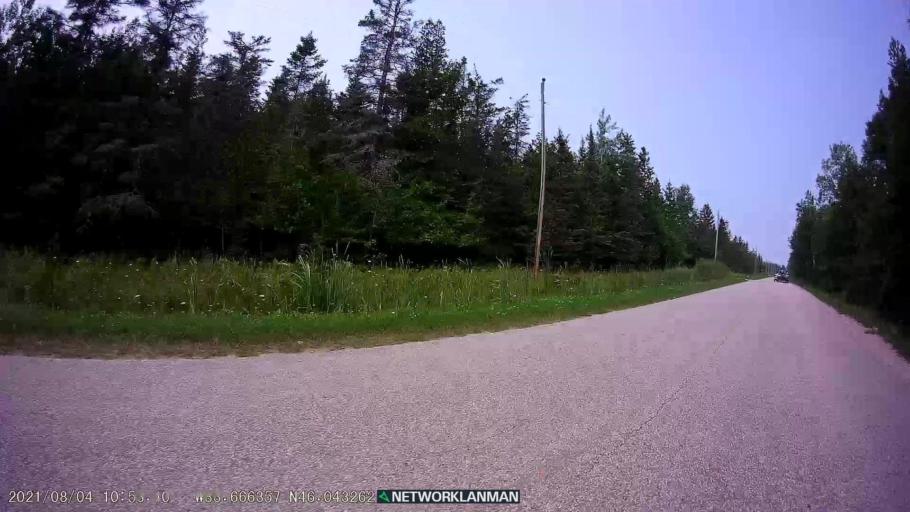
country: CA
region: Ontario
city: Thessalon
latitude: 46.0440
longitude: -83.6669
